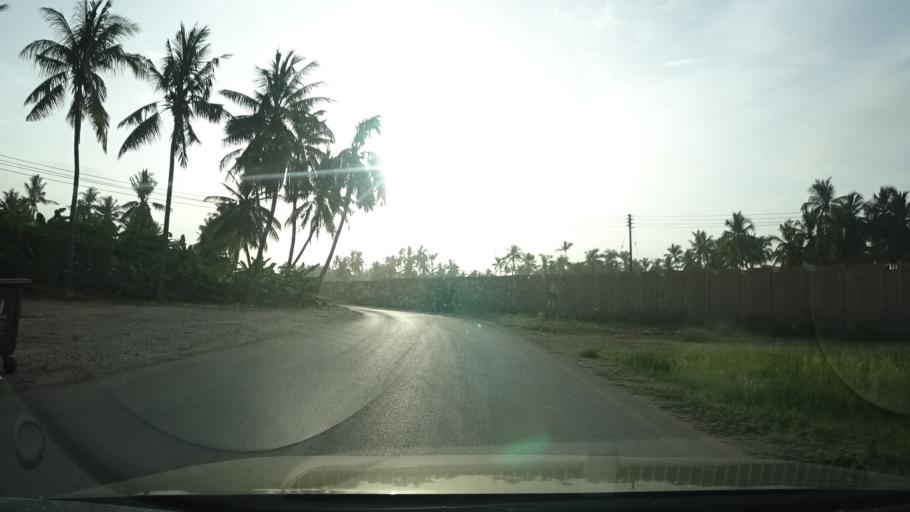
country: OM
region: Zufar
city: Salalah
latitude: 17.0182
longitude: 54.1434
